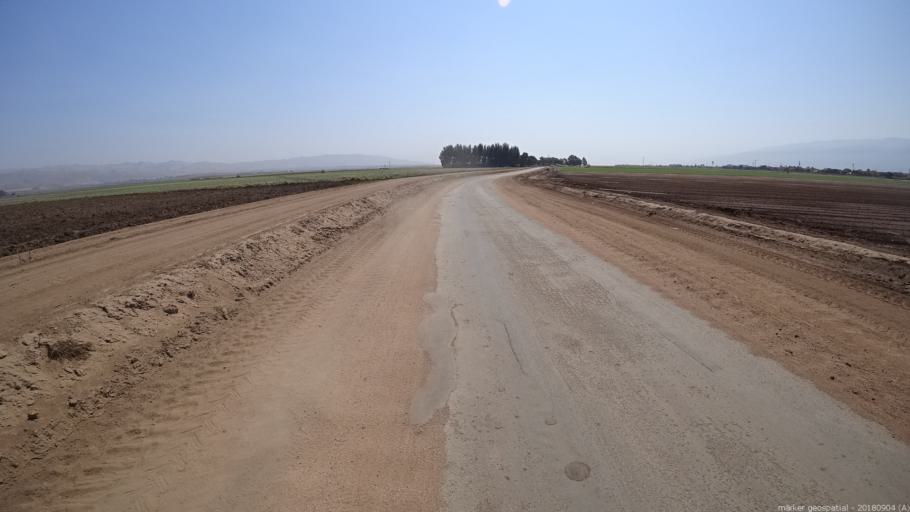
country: US
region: California
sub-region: Monterey County
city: Gonzales
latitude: 36.5304
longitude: -121.4450
